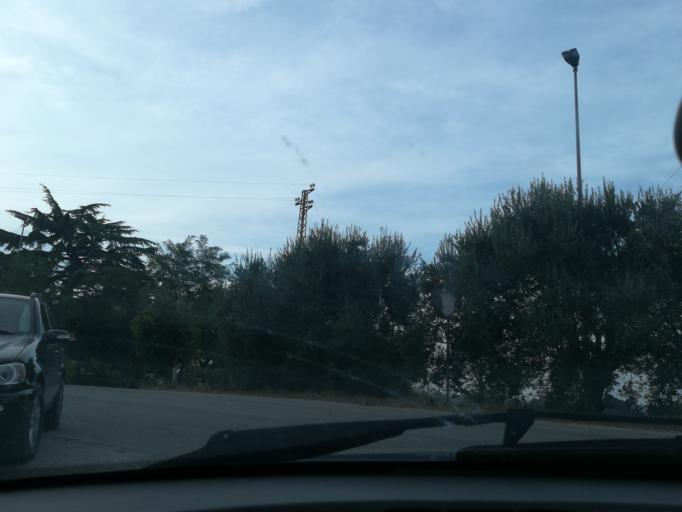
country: IT
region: The Marches
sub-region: Provincia di Macerata
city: Piediripa
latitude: 43.2962
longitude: 13.4831
